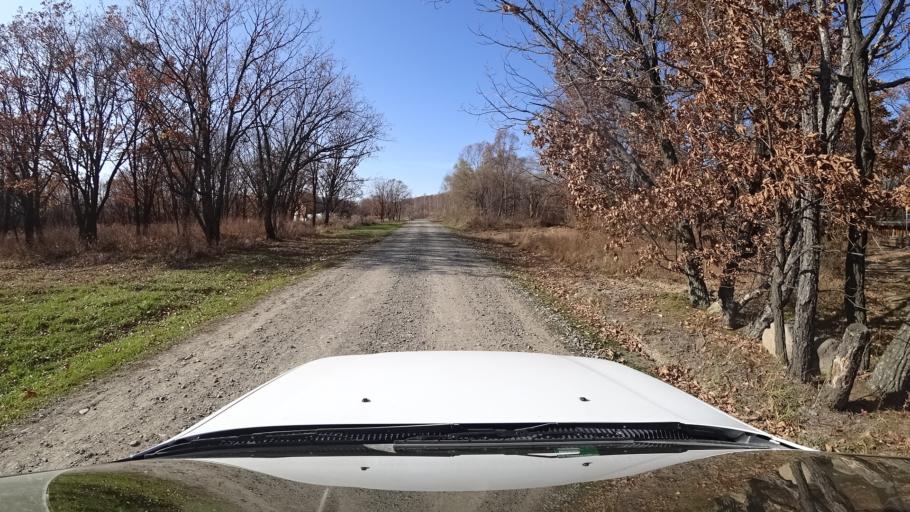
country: RU
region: Primorskiy
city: Dal'nerechensk
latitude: 45.8824
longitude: 133.7246
